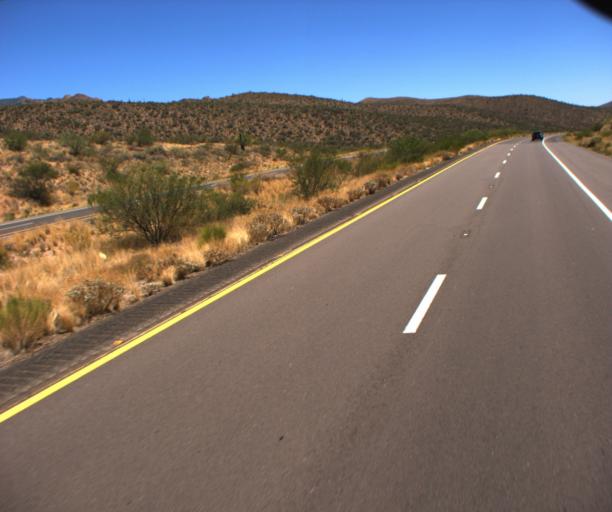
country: US
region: Arizona
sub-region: Maricopa County
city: Rio Verde
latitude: 33.7879
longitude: -111.4940
